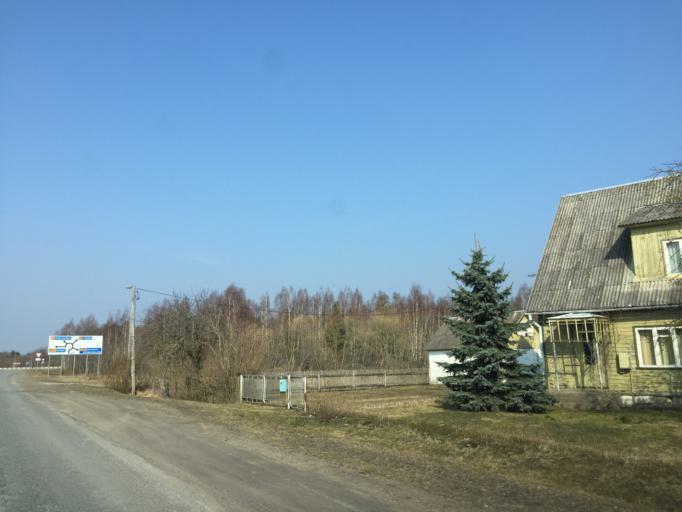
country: EE
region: Saare
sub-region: Kuressaare linn
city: Kuressaare
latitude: 58.2667
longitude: 22.4702
